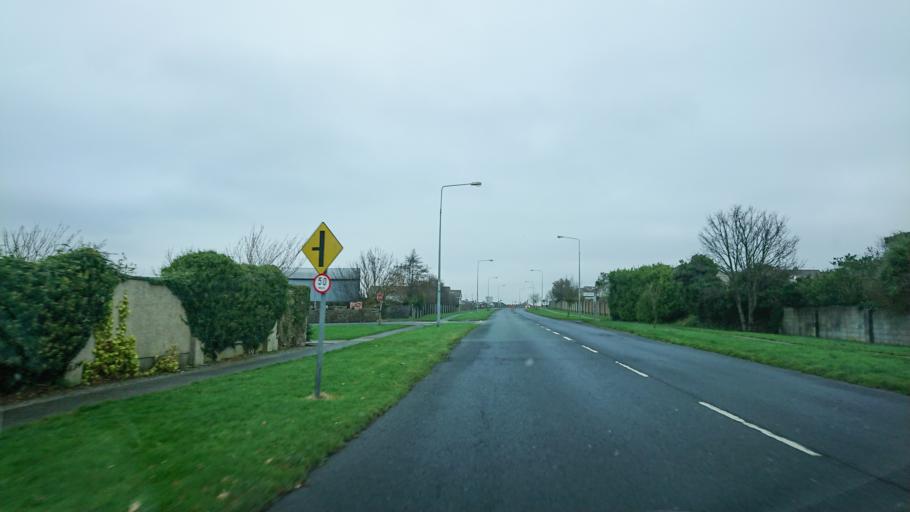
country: IE
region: Munster
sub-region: Waterford
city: Tra Mhor
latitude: 52.1639
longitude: -7.1656
